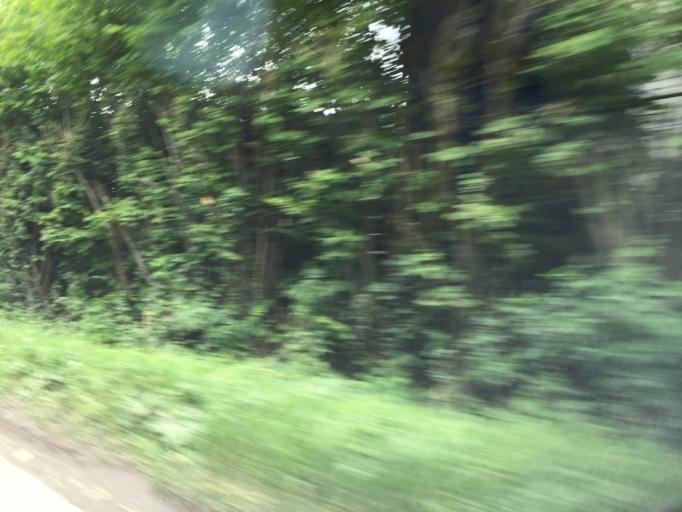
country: GB
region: England
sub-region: Wiltshire
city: Minety
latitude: 51.6473
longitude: -1.9844
